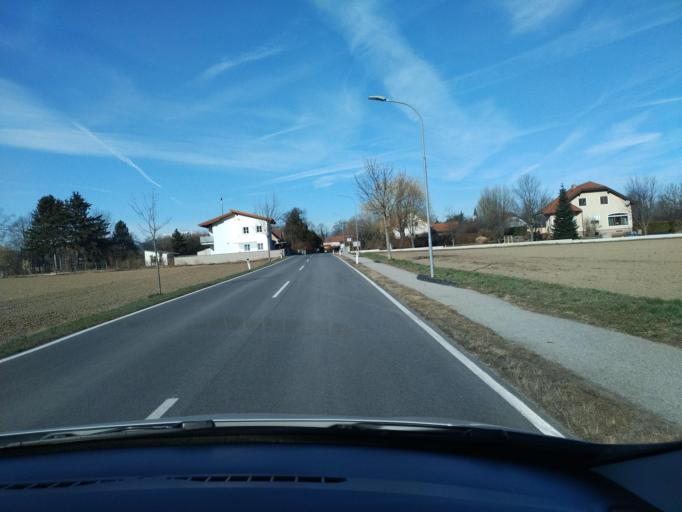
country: AT
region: Lower Austria
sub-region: Politischer Bezirk Wiener Neustadt
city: Lanzenkirchen
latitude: 47.7390
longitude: 16.2453
